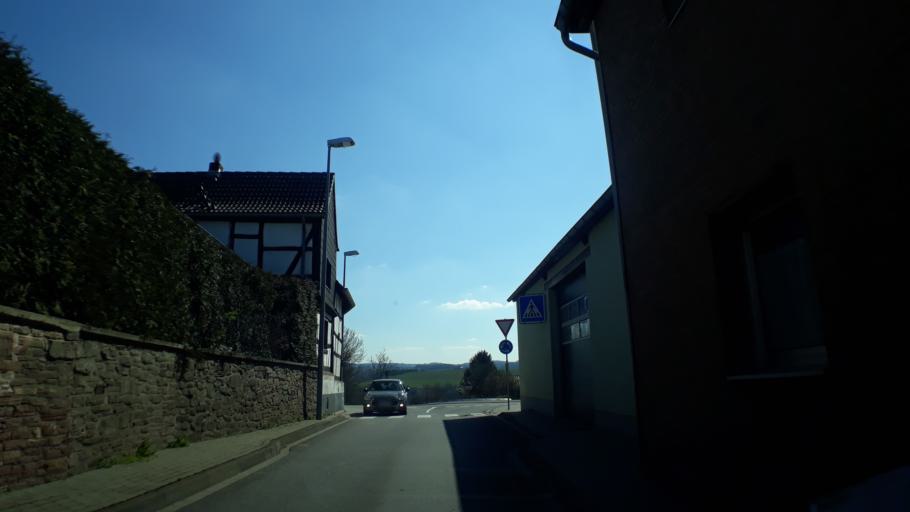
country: DE
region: North Rhine-Westphalia
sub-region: Regierungsbezirk Koln
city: Mechernich
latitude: 50.5685
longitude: 6.6498
